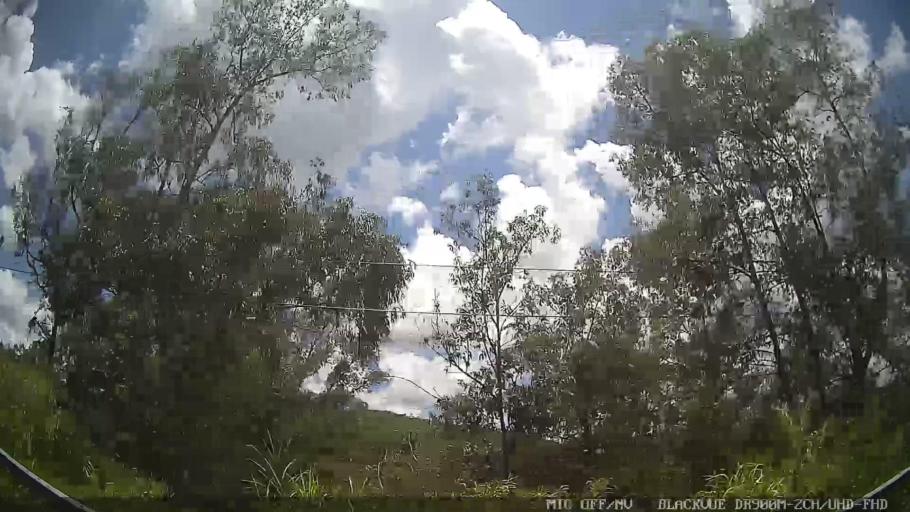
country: BR
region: Sao Paulo
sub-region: Amparo
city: Amparo
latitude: -22.6556
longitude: -46.7443
